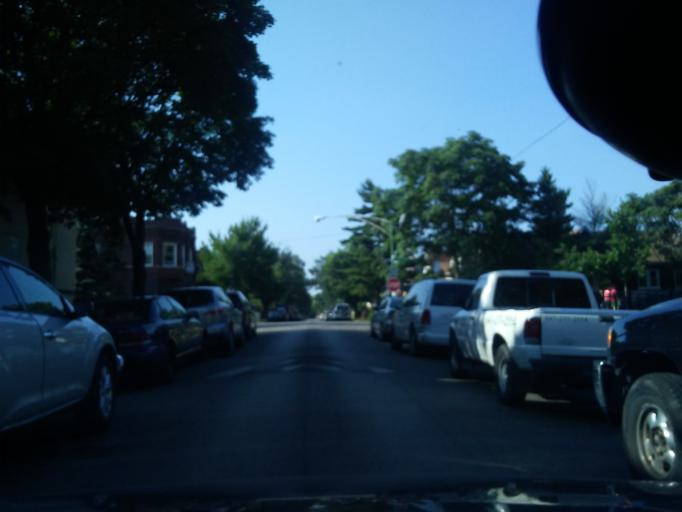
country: US
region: Illinois
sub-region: Cook County
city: Oak Park
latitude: 41.9228
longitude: -87.7511
